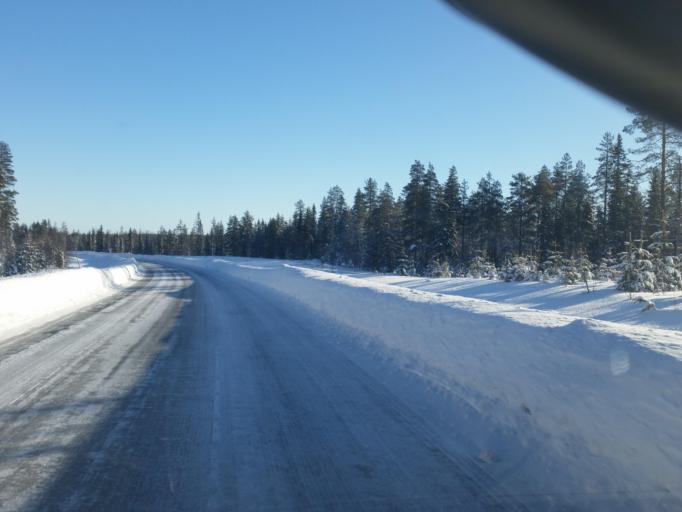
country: SE
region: Vaesterbotten
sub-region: Skelleftea Kommun
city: Storvik
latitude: 65.3239
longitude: 20.7704
